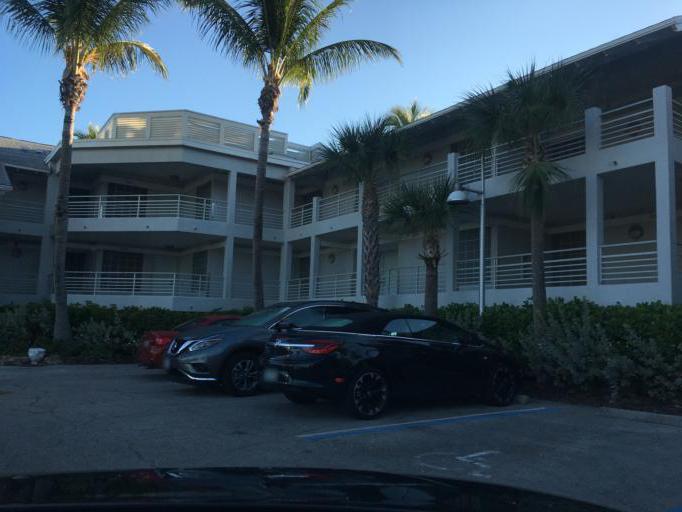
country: US
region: Florida
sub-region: Lee County
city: Pine Island Center
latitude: 26.5491
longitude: -82.1960
